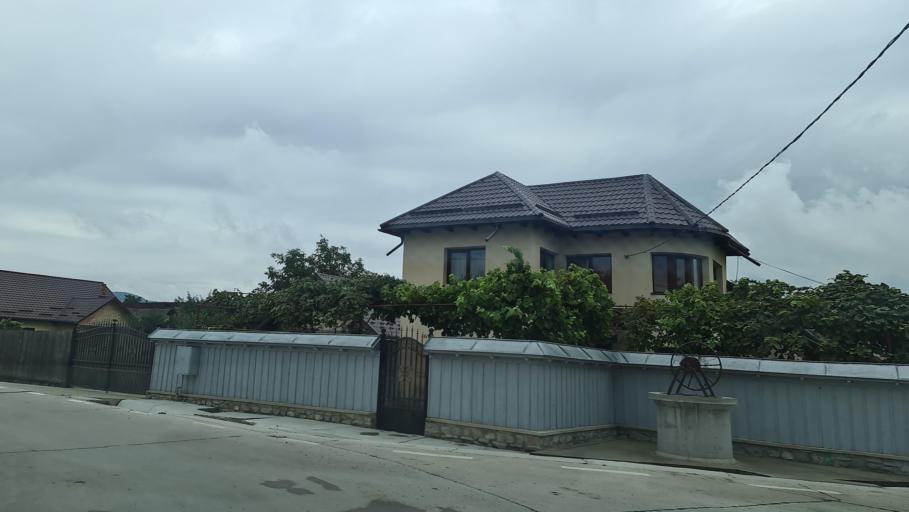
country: RO
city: Vanatori-Neamt
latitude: 47.2109
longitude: 26.3145
